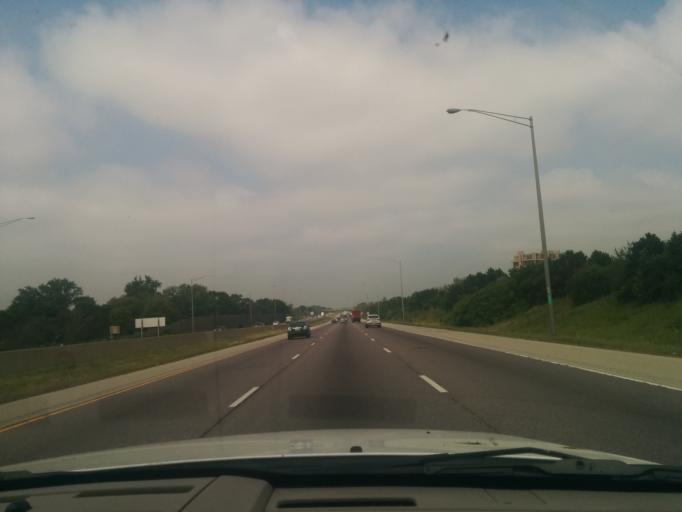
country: US
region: Illinois
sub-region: DuPage County
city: Addison
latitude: 41.9435
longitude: -87.9909
